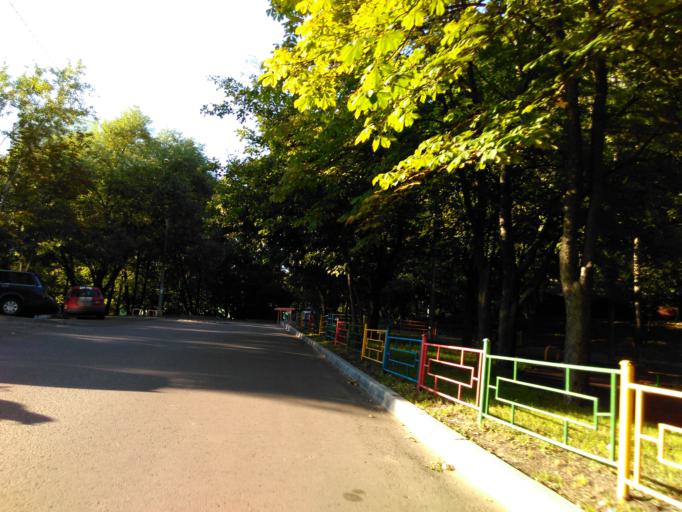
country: RU
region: Moscow
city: Tyoply Stan
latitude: 55.6329
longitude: 37.5110
